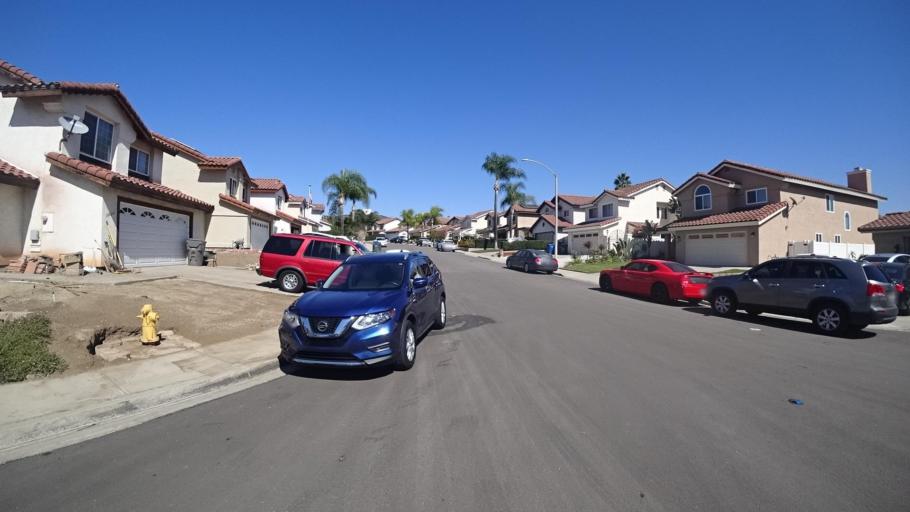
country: US
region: California
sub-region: San Diego County
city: Rancho San Diego
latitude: 32.7491
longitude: -116.9381
